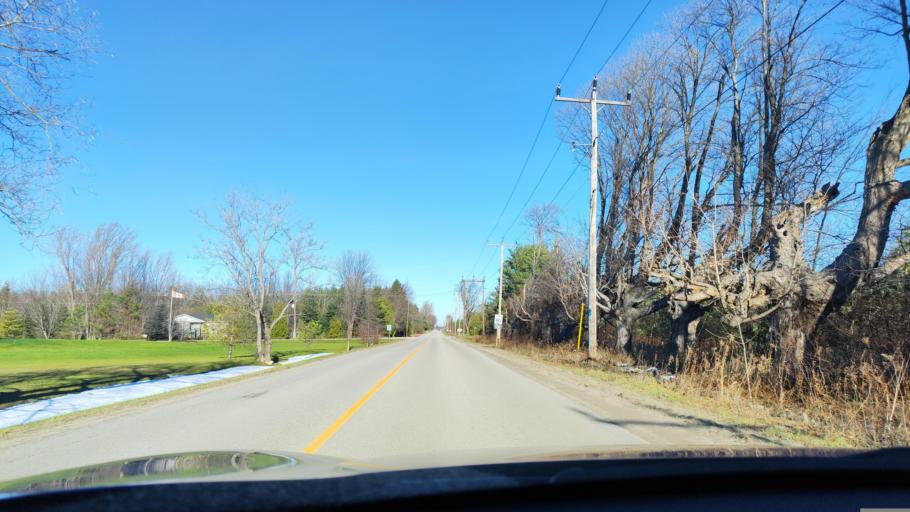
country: CA
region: Ontario
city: Collingwood
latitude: 44.4686
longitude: -80.1746
